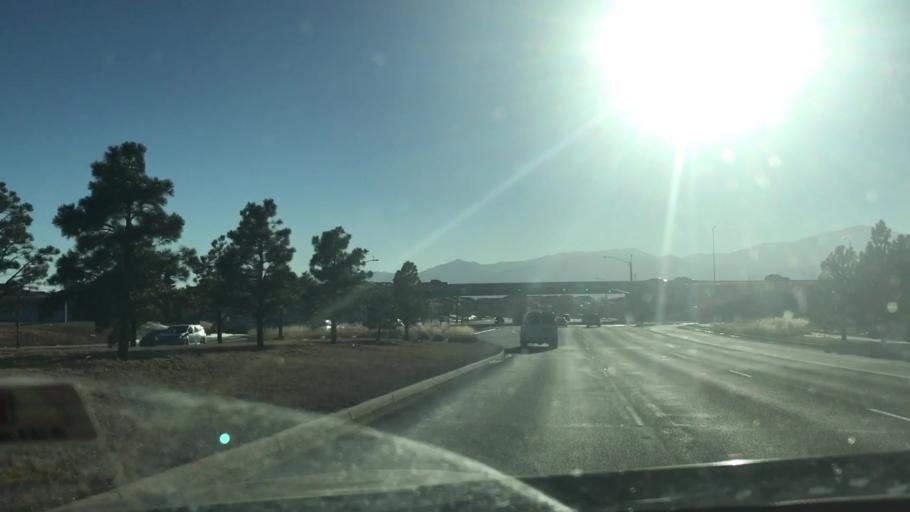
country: US
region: Colorado
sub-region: El Paso County
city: Black Forest
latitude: 38.9698
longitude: -104.7420
